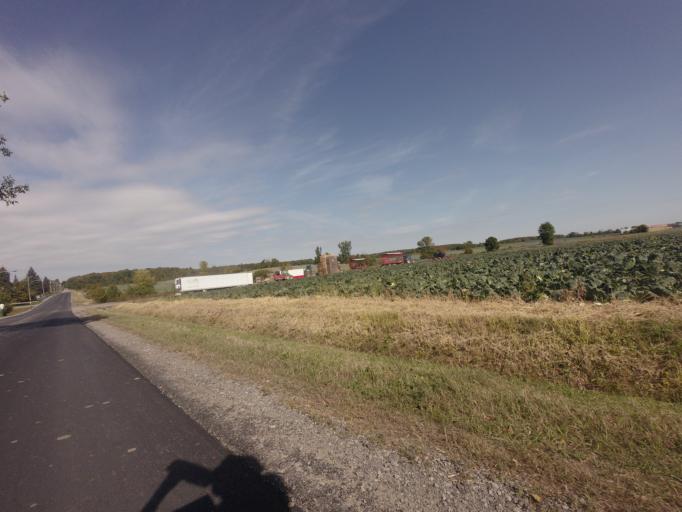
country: CA
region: Quebec
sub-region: Laurentides
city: Saint-Eustache
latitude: 45.5968
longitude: -73.9163
